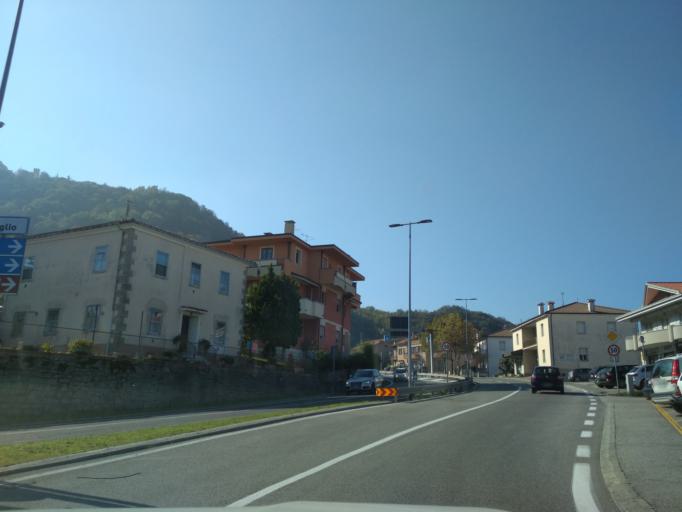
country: SM
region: Borgo Maggiore
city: Borgo Maggiore
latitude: 43.9434
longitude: 12.4456
